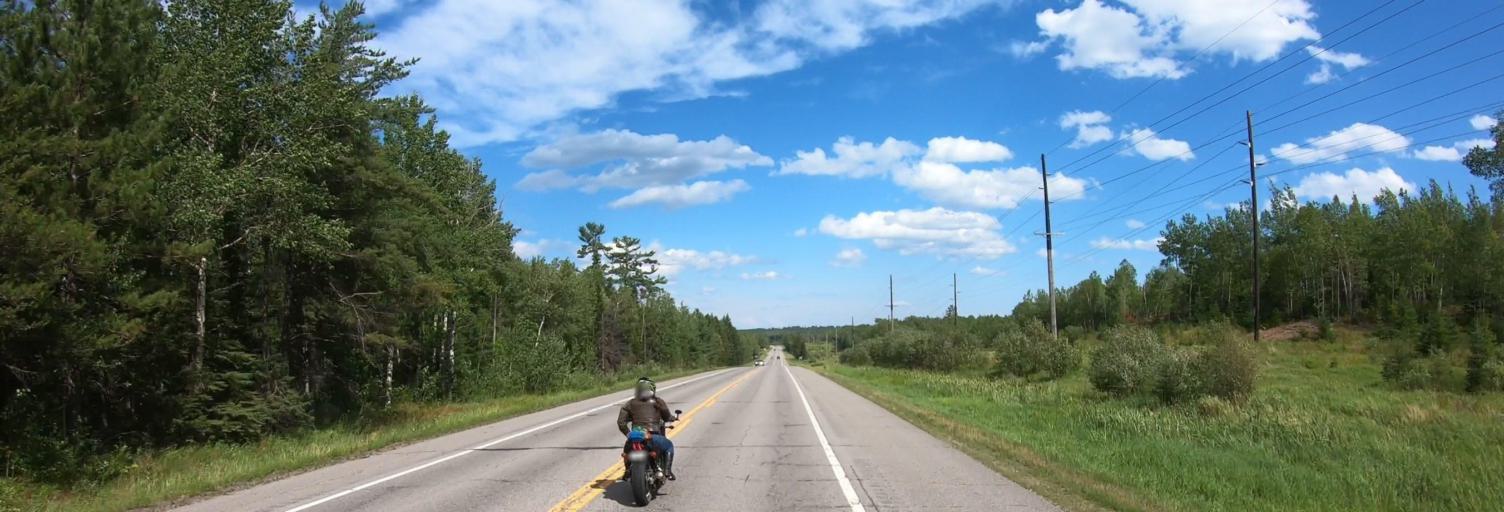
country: US
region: Minnesota
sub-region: Saint Louis County
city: Aurora
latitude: 47.7975
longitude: -92.3279
